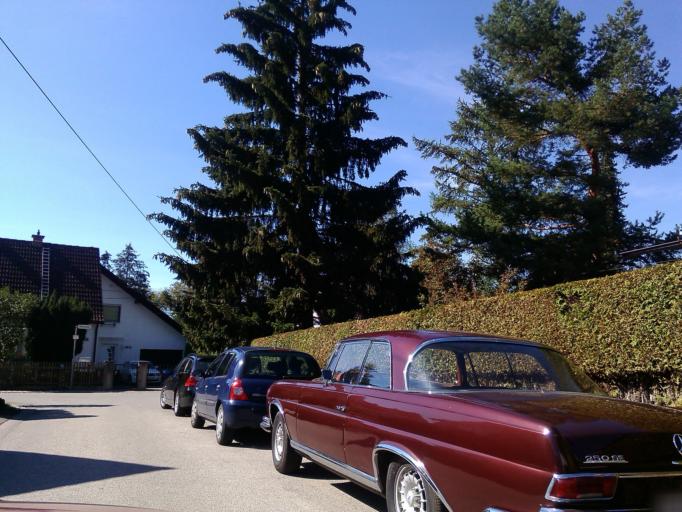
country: DE
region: Bavaria
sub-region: Upper Bavaria
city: Gauting
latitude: 48.0772
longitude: 11.3489
